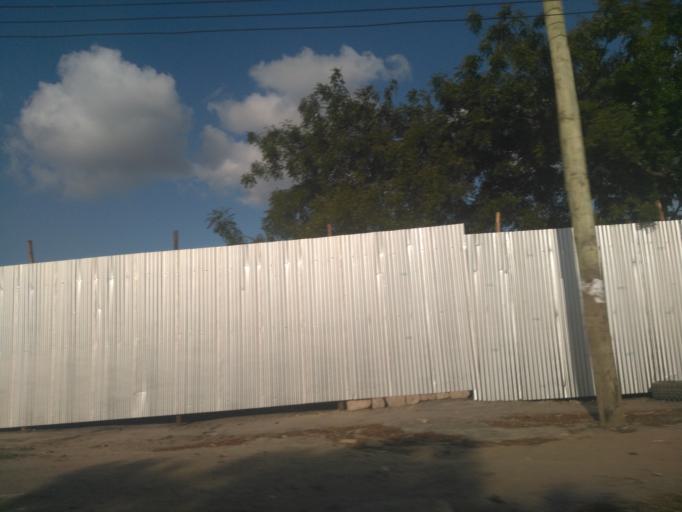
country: TZ
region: Dar es Salaam
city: Dar es Salaam
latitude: -6.8567
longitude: 39.2610
